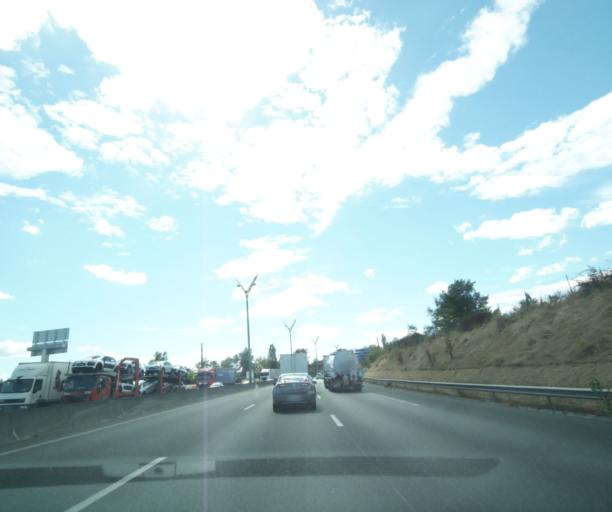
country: FR
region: Aquitaine
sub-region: Departement de la Gironde
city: Villenave-d'Ornon
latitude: 44.7840
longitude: -0.5423
